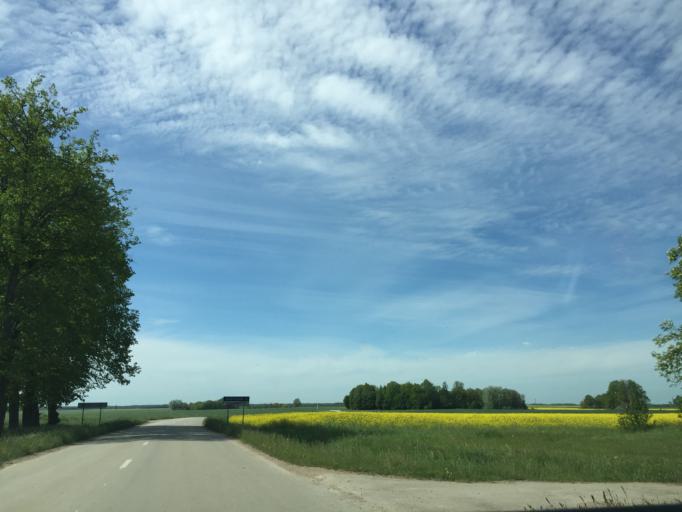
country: LT
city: Linkuva
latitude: 56.0986
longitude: 24.1296
